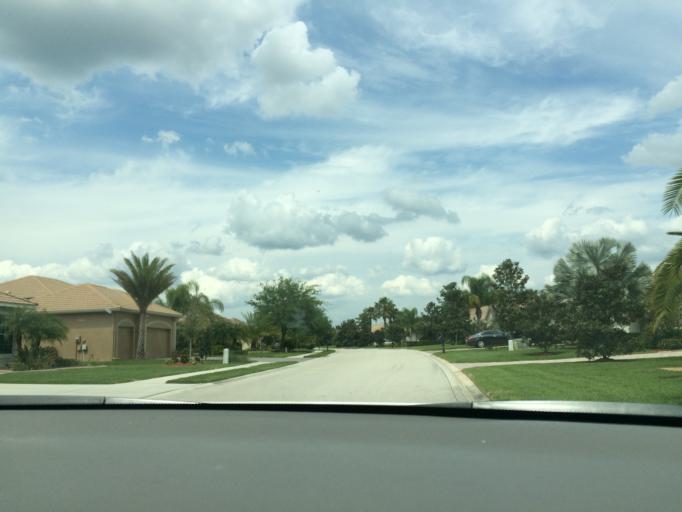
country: US
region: Florida
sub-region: Manatee County
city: Ellenton
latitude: 27.5000
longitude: -82.4126
